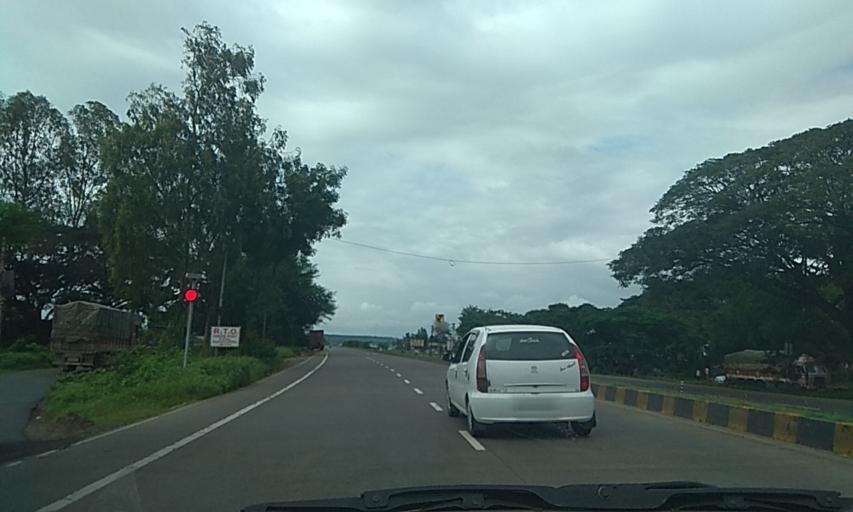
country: IN
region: Maharashtra
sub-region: Kolhapur
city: Kagal
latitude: 16.5673
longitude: 74.3160
